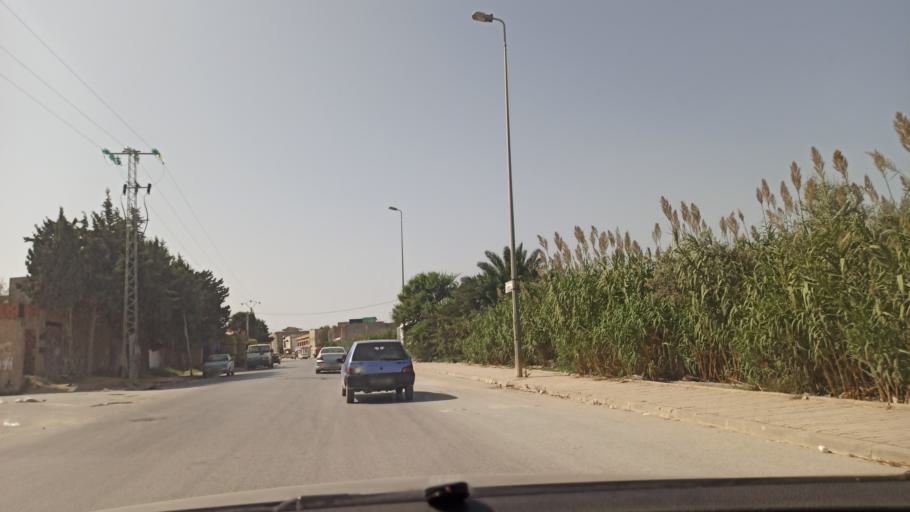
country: TN
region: Manouba
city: Manouba
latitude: 36.7582
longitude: 10.1047
